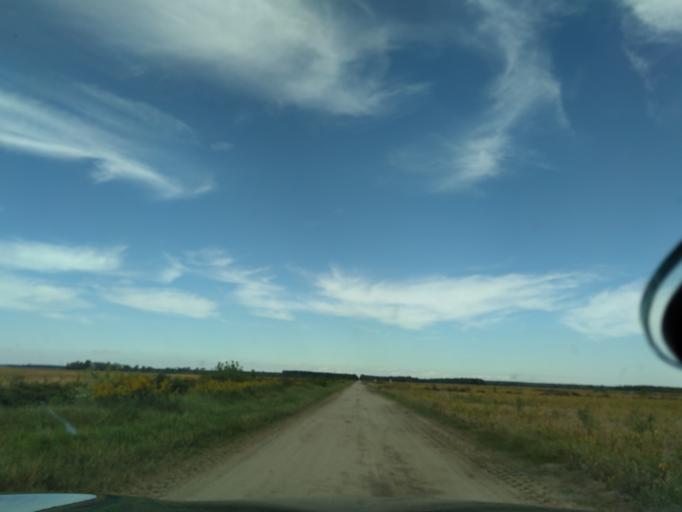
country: US
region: North Carolina
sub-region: Beaufort County
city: Belhaven
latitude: 35.6992
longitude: -76.5905
